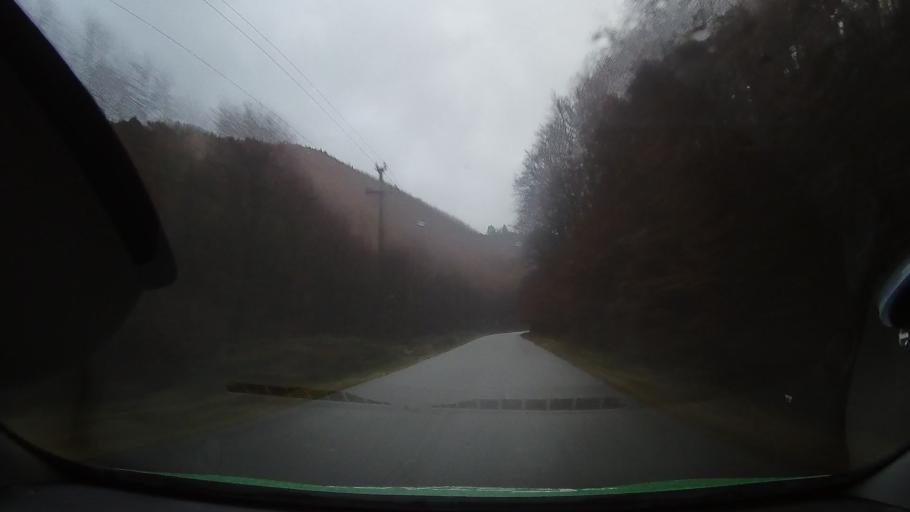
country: RO
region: Hunedoara
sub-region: Comuna Ribita
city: Ribita
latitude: 46.2785
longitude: 22.7394
